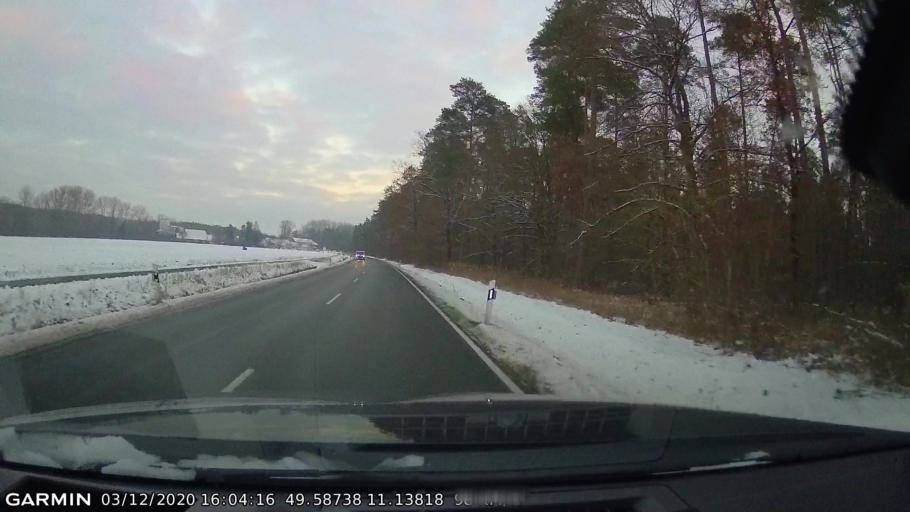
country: DE
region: Bavaria
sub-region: Upper Franconia
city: Kleinsendelbach
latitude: 49.5874
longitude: 11.1384
